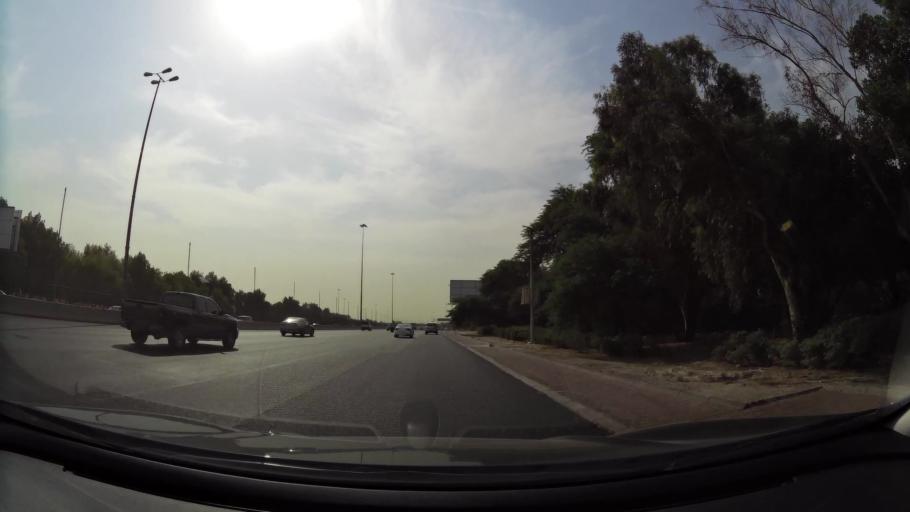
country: KW
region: Al Farwaniyah
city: Janub as Surrah
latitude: 29.2733
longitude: 47.9865
